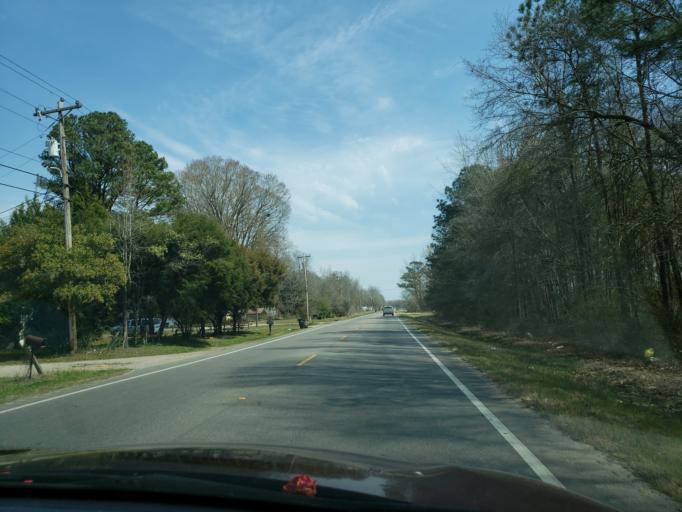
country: US
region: Alabama
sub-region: Autauga County
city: Prattville
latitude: 32.4338
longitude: -86.4838
